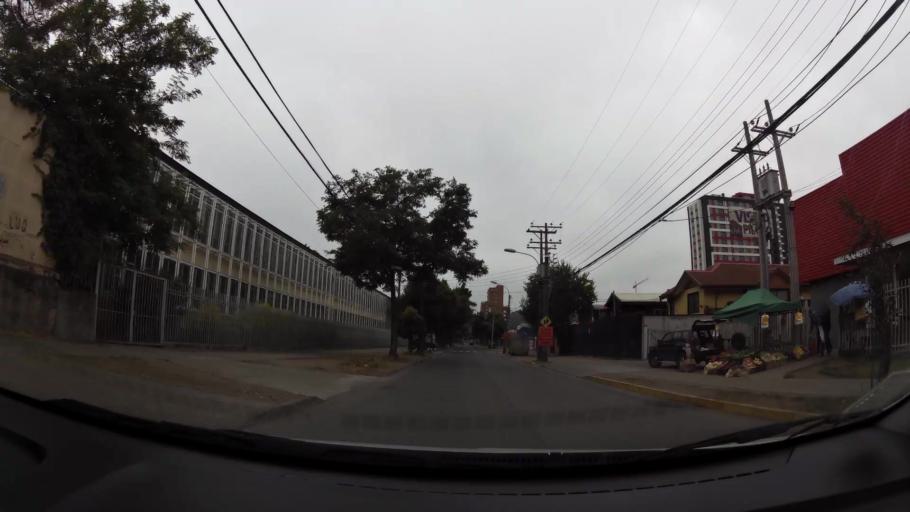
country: CL
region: Biobio
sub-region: Provincia de Concepcion
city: Concepcion
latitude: -36.8149
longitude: -73.0397
